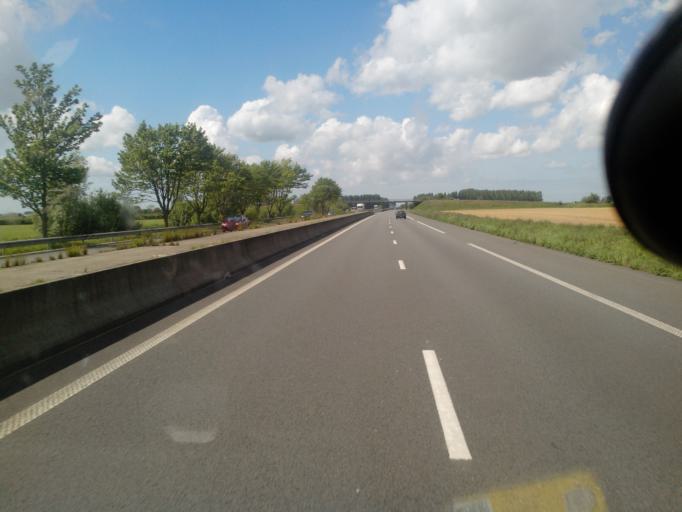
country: FR
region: Nord-Pas-de-Calais
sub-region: Departement du Nord
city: Quaedypre
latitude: 50.9165
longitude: 2.4799
